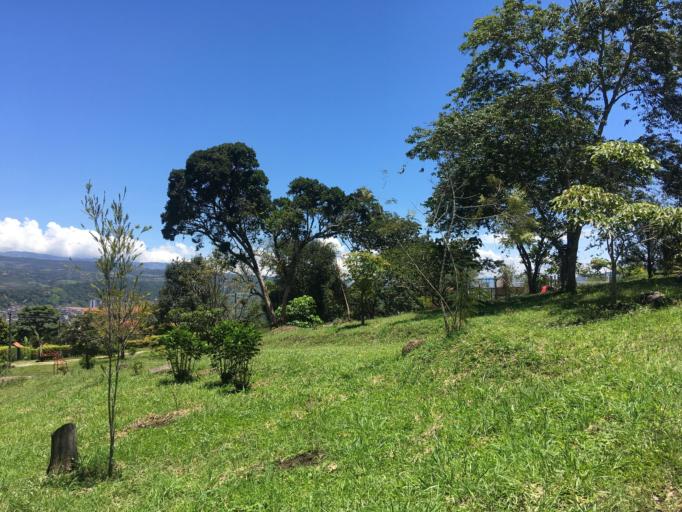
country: CO
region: Santander
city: Barbosa
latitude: 5.9181
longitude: -73.6045
